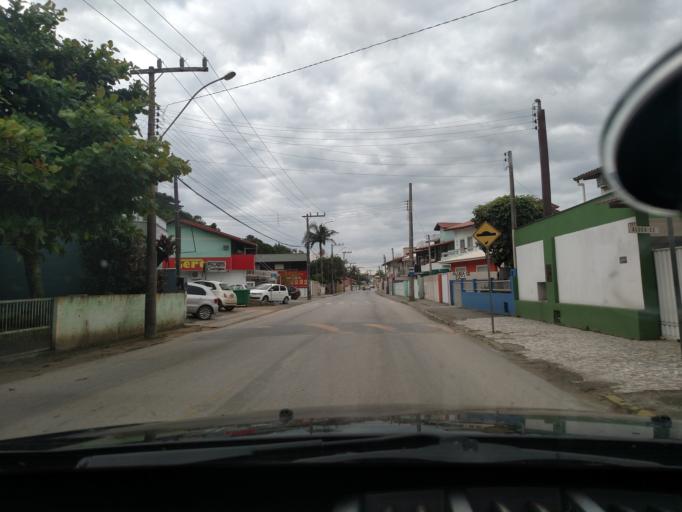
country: BR
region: Santa Catarina
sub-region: Porto Belo
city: Porto Belo
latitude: -27.1805
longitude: -48.5233
